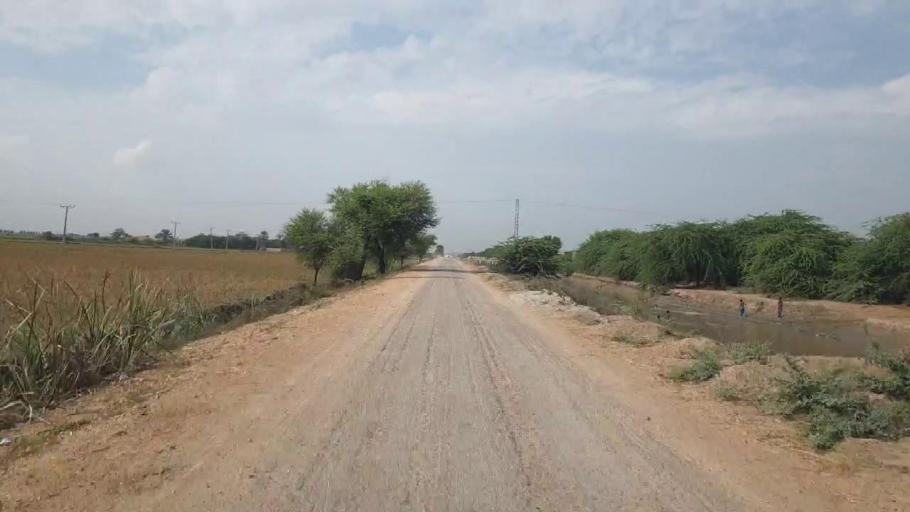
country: PK
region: Sindh
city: Kario
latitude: 24.6323
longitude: 68.5702
